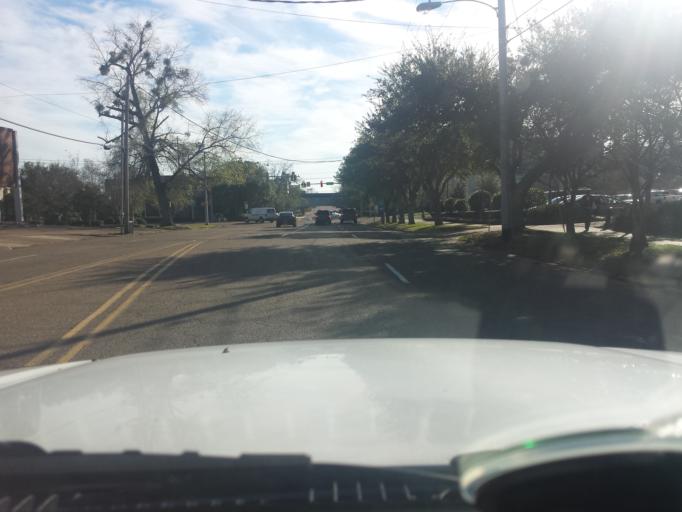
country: US
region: Mississippi
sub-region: Hinds County
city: Jackson
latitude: 32.3054
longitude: -90.1792
